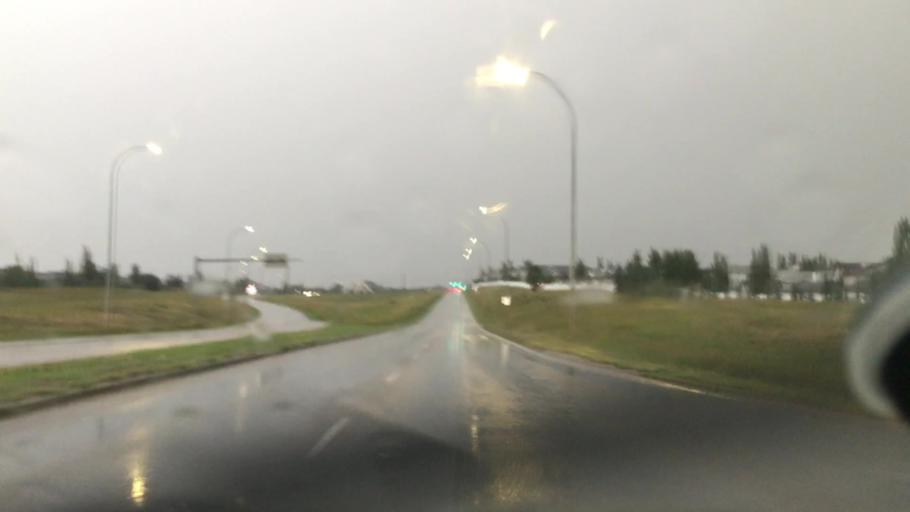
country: CA
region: Alberta
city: Edmonton
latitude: 53.4516
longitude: -113.5896
